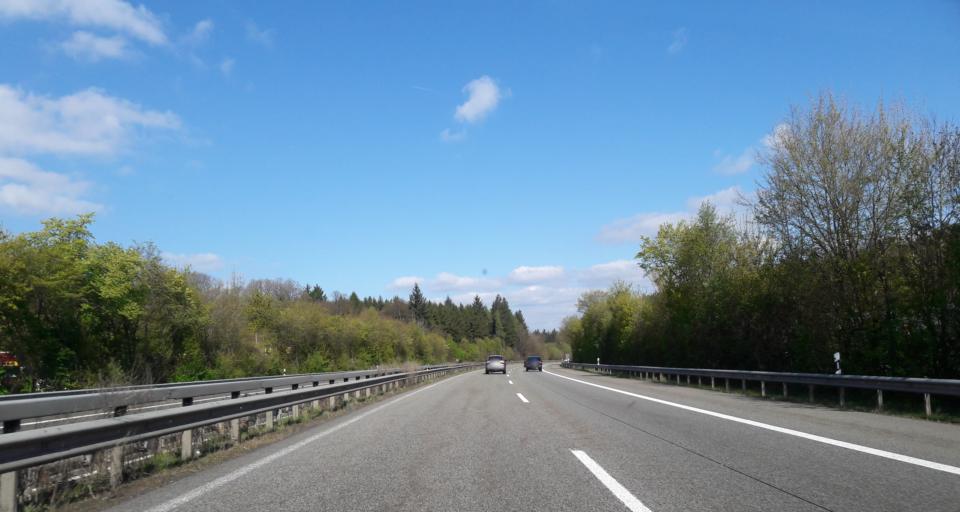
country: DE
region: Rheinland-Pfalz
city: Niederofflingen
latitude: 50.0690
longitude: 6.8813
